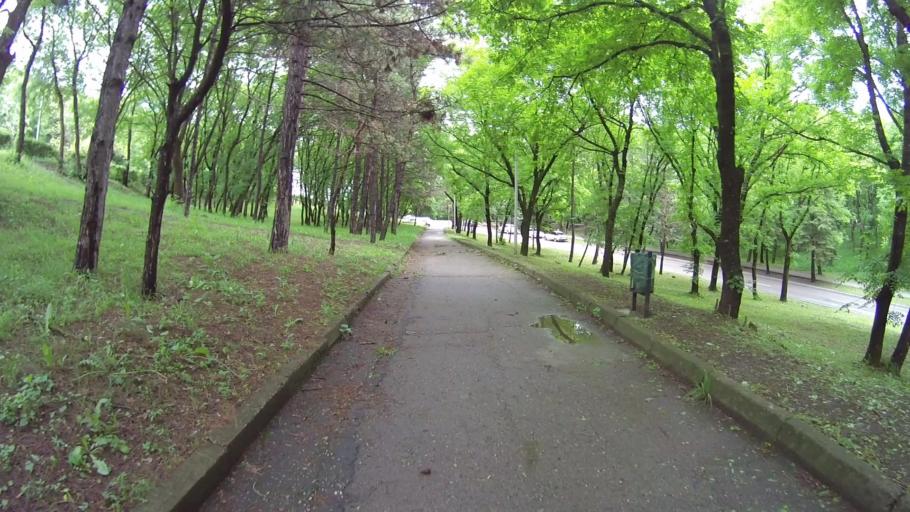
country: RU
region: Stavropol'skiy
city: Goryachevodskiy
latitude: 44.0414
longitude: 43.0852
